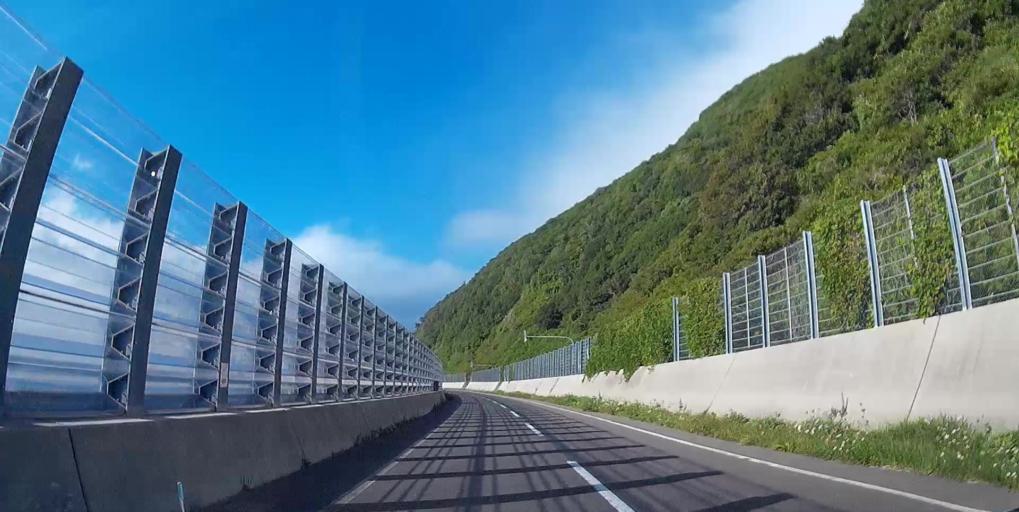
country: JP
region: Hokkaido
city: Iwanai
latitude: 42.3344
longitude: 139.7756
